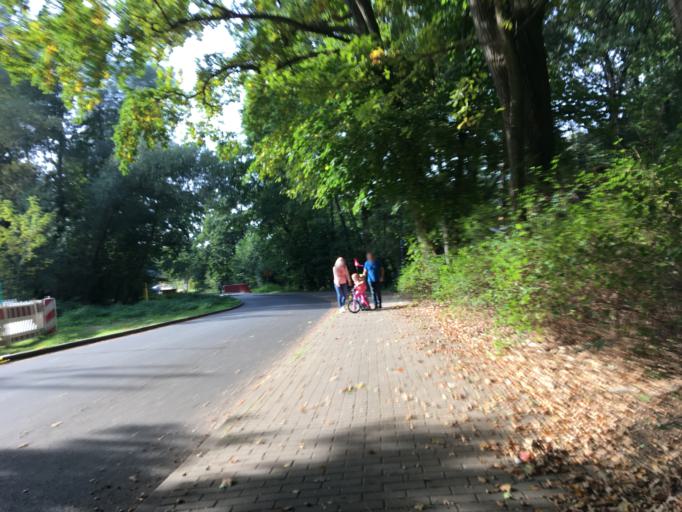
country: DE
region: Brandenburg
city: Hoppegarten
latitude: 52.5175
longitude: 13.6620
